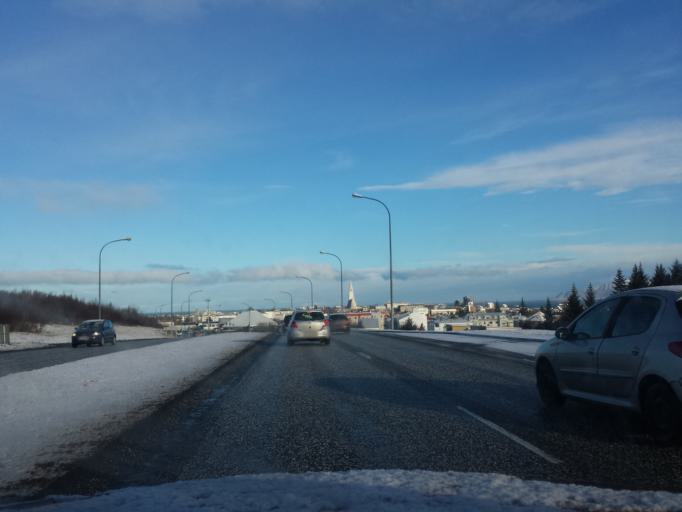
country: IS
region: Capital Region
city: Kopavogur
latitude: 64.1289
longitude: -21.9117
